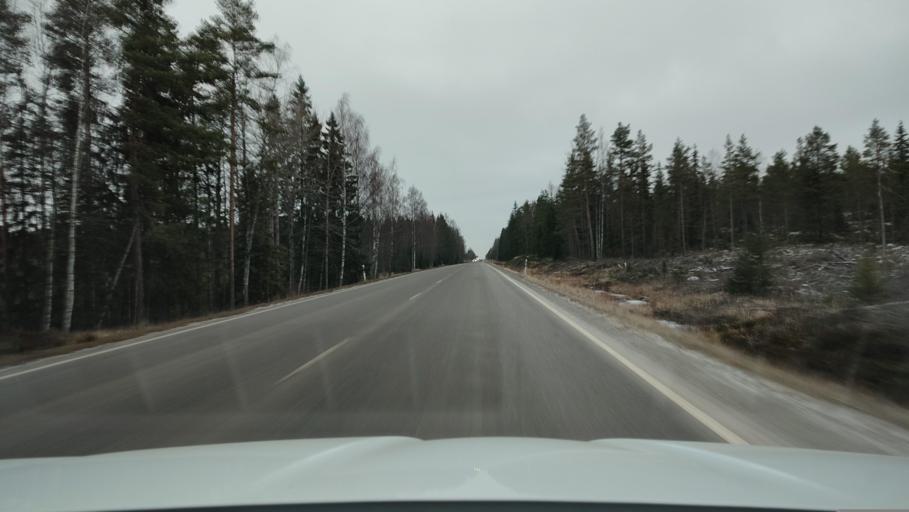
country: FI
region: Ostrobothnia
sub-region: Sydosterbotten
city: Naerpes
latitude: 62.4913
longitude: 21.4444
